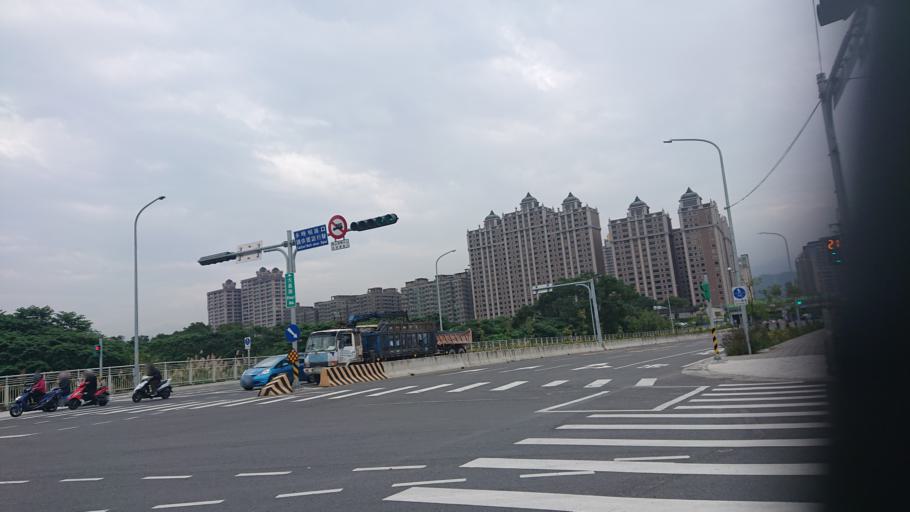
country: TW
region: Taiwan
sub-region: Taoyuan
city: Taoyuan
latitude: 24.9525
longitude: 121.3748
